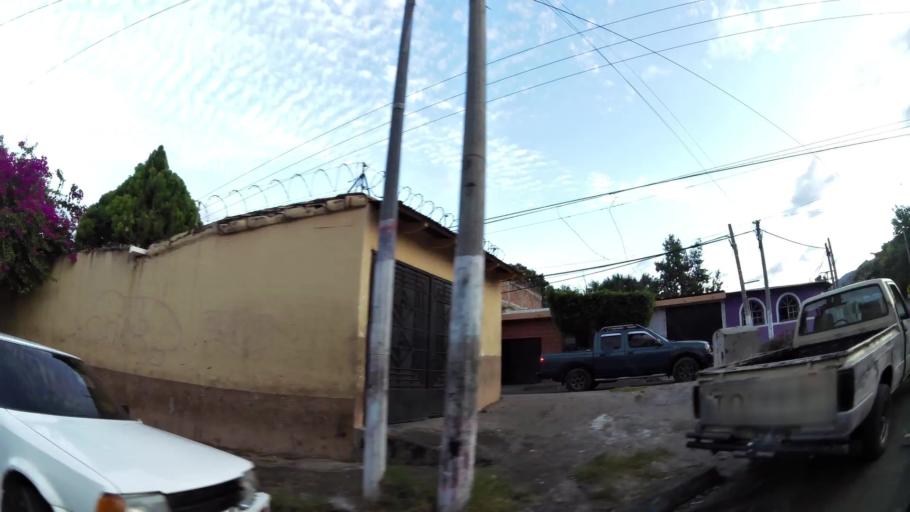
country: SV
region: San Vicente
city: San Vicente
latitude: 13.6457
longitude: -88.7888
